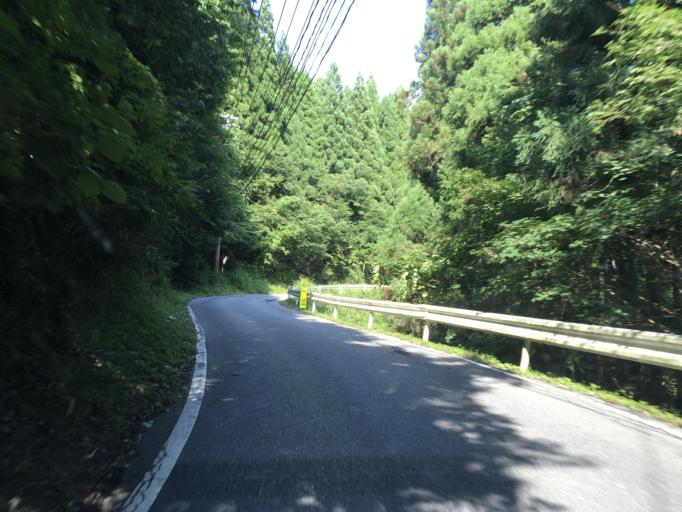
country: JP
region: Iwate
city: Ofunato
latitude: 38.9175
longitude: 141.6088
